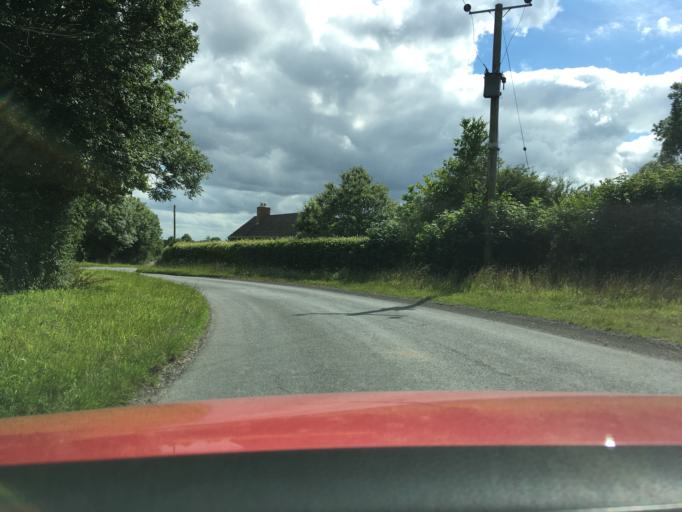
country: GB
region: England
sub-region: Gloucestershire
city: Stonehouse
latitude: 51.8319
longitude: -2.3421
